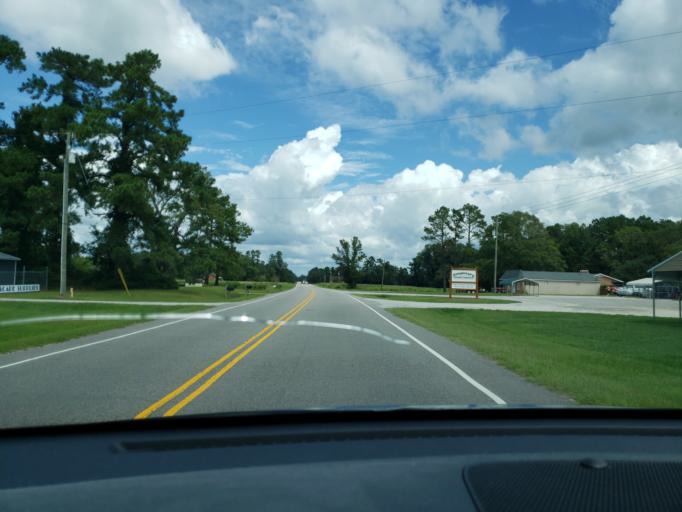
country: US
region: North Carolina
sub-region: Columbus County
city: Brunswick
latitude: 34.2156
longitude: -78.7570
